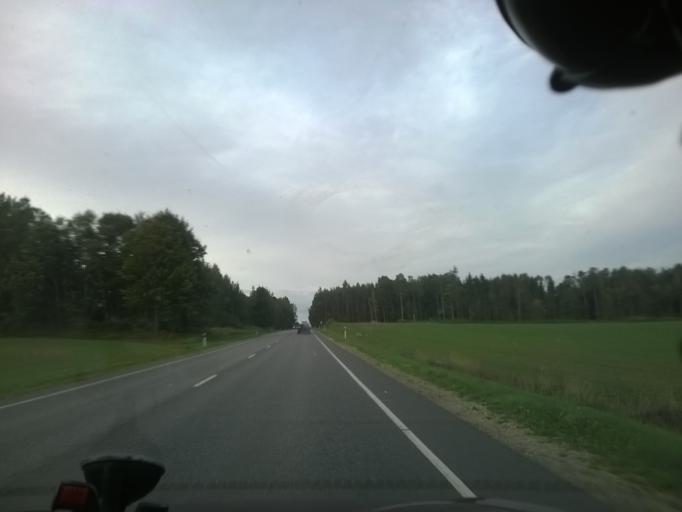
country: EE
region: Tartu
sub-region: UElenurme vald
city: Ulenurme
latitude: 58.0489
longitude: 26.7296
